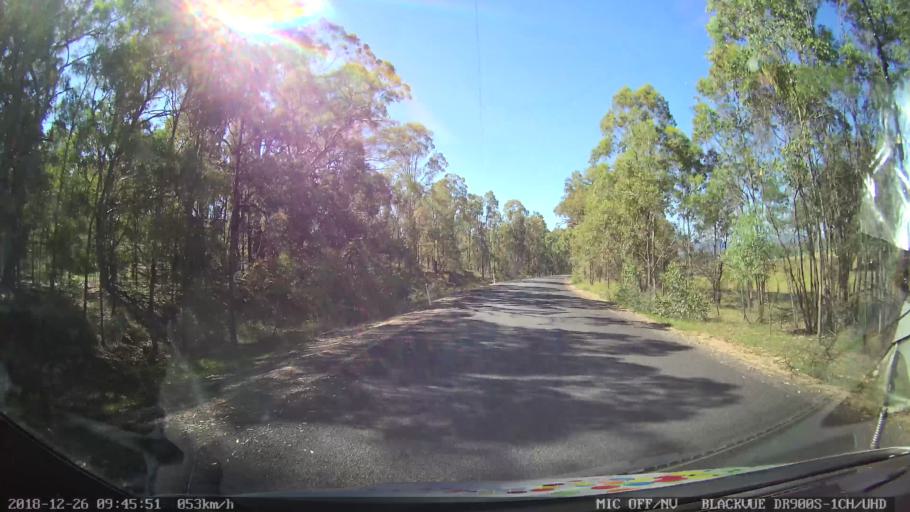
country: AU
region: New South Wales
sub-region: Mid-Western Regional
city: Kandos
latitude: -32.9643
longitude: 150.1060
